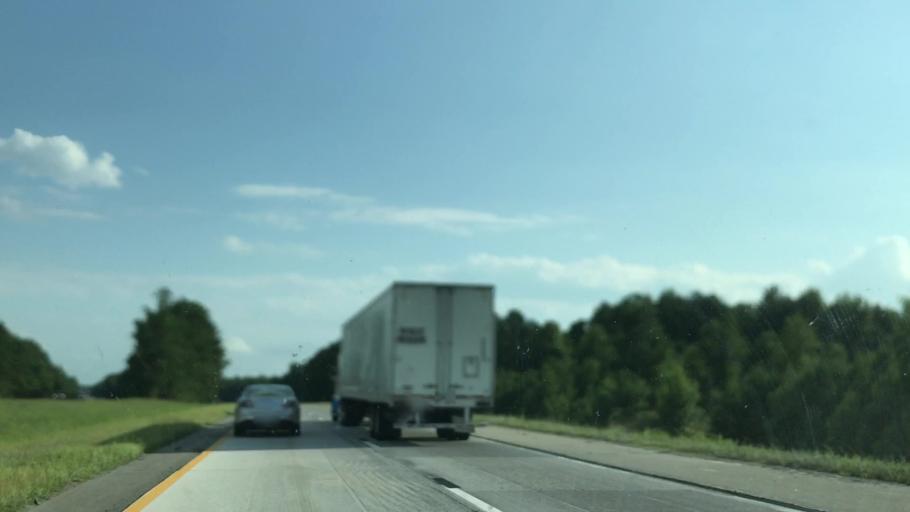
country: US
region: South Carolina
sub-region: Dorchester County
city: Saint George
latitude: 33.1272
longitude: -80.6395
